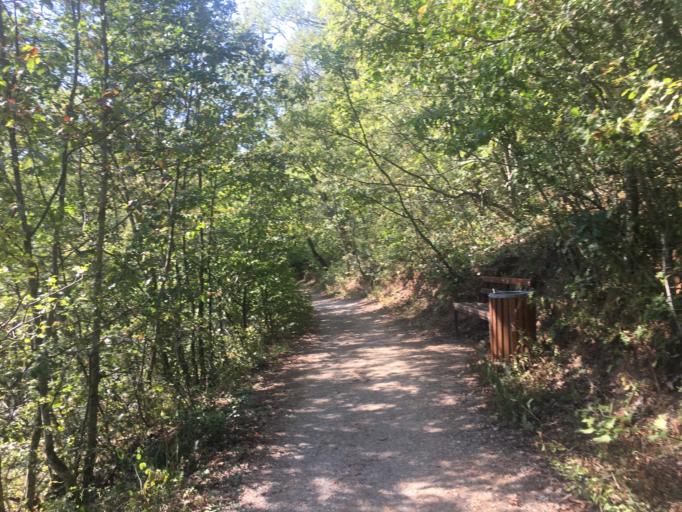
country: XK
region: Pristina
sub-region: Komuna e Prishtines
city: Pristina
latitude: 42.6647
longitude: 21.2195
